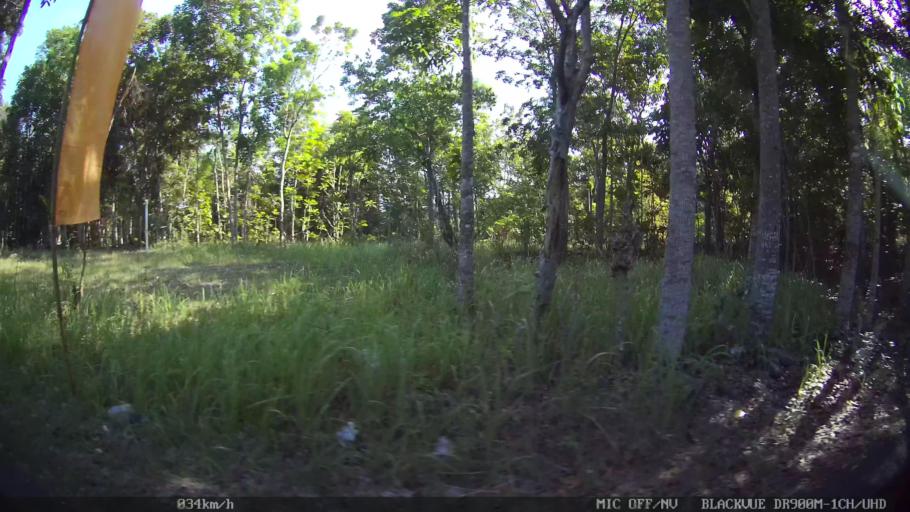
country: ID
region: Daerah Istimewa Yogyakarta
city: Kasihan
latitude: -7.8355
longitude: 110.2843
